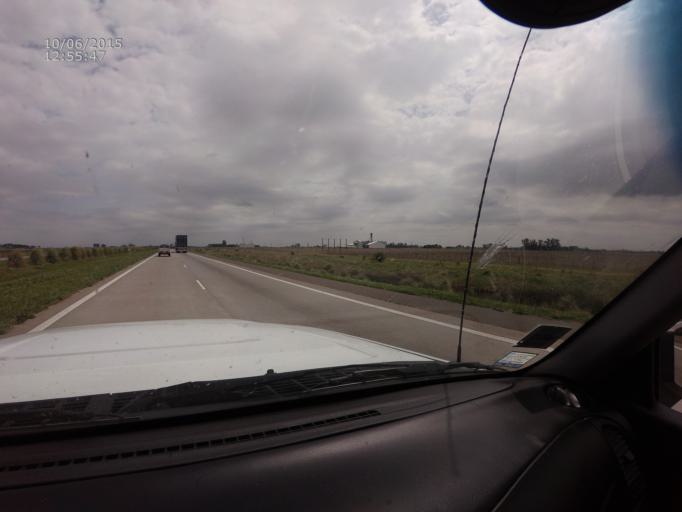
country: AR
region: Santa Fe
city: Armstrong
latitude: -32.8103
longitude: -61.6015
